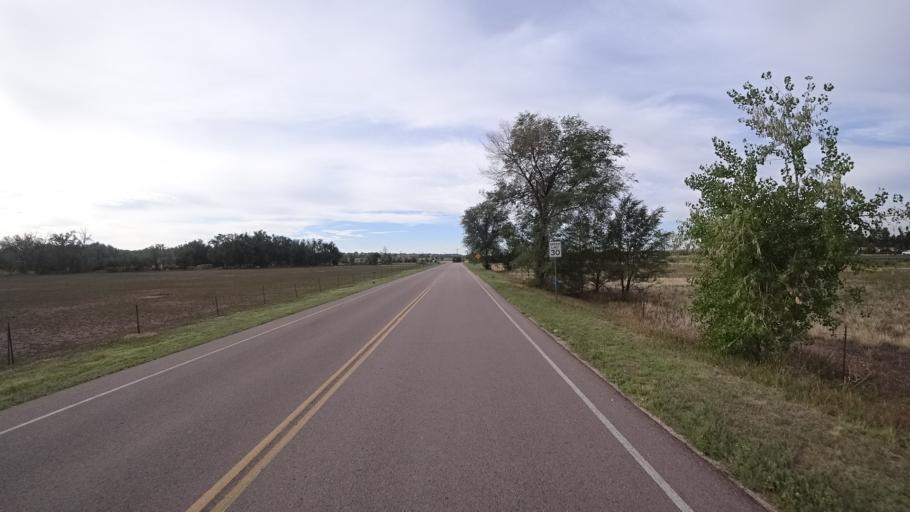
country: US
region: Colorado
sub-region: El Paso County
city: Security-Widefield
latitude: 38.7176
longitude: -104.7139
